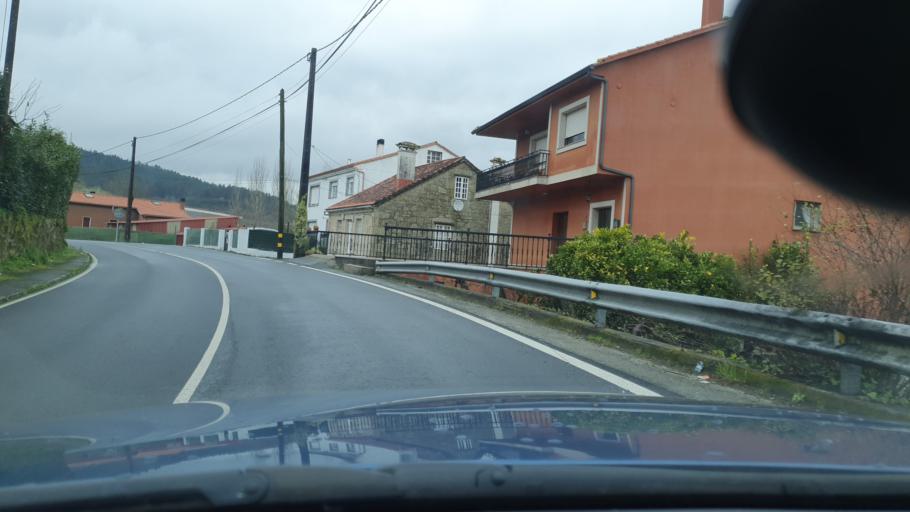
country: ES
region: Galicia
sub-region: Provincia da Coruna
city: Padron
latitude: 42.7499
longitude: -8.6692
